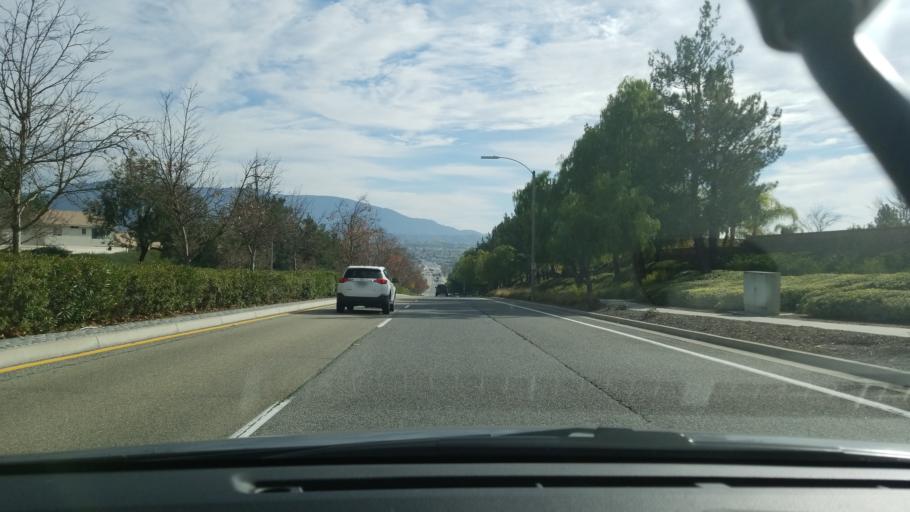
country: US
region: California
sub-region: Riverside County
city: Temecula
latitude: 33.4932
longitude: -117.0822
